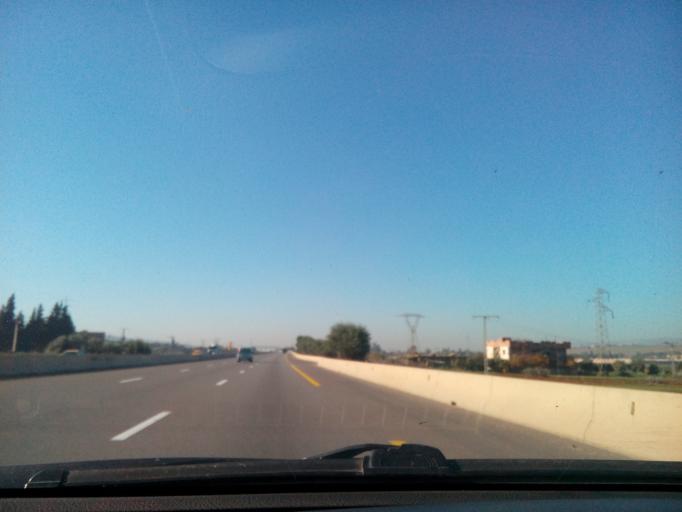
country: DZ
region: Chlef
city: Boukadir
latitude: 36.0343
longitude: 1.0781
